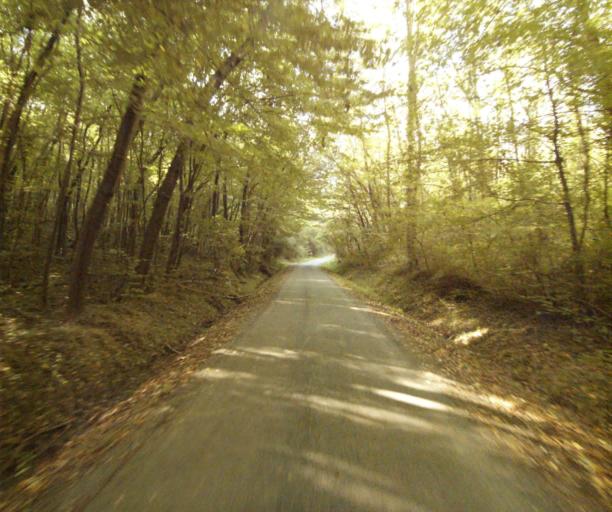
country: FR
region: Midi-Pyrenees
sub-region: Departement du Tarn-et-Garonne
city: Nohic
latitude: 43.9238
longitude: 1.4449
